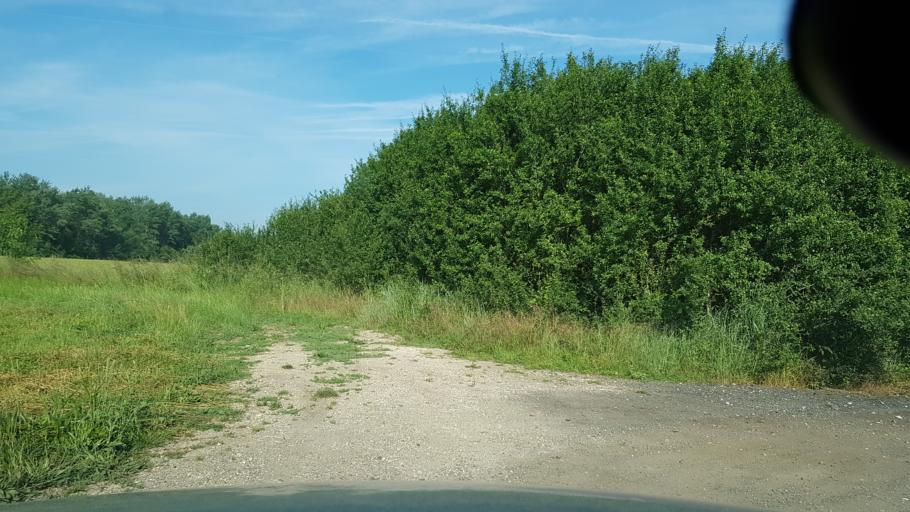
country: FR
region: Centre
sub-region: Departement du Loir-et-Cher
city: Selles-sur-Cher
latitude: 47.2727
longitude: 1.5517
